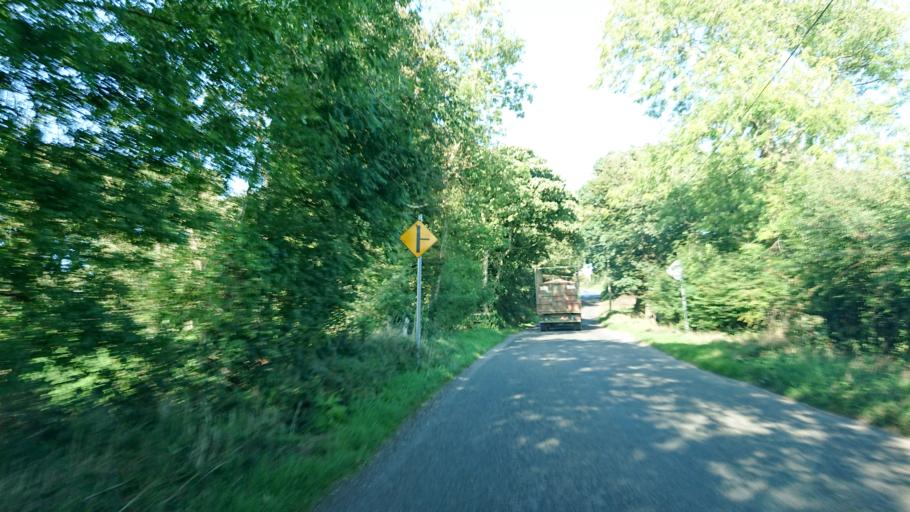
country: IE
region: Munster
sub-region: Waterford
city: Dunmore East
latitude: 52.1823
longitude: -7.0056
